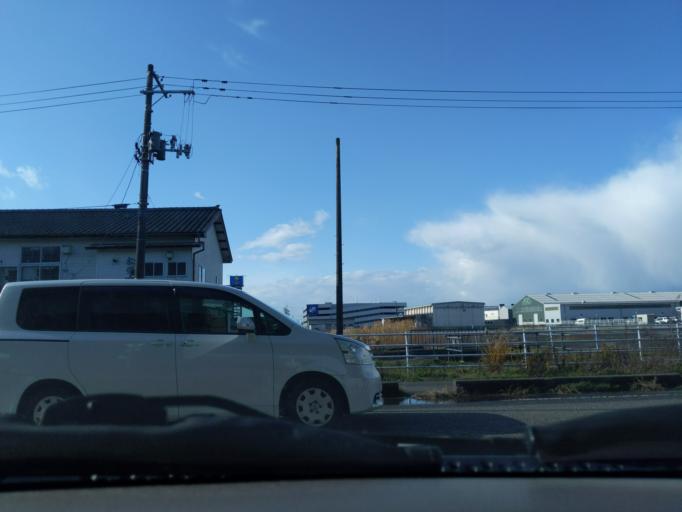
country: JP
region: Niigata
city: Kameda-honcho
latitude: 37.8701
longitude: 139.0874
